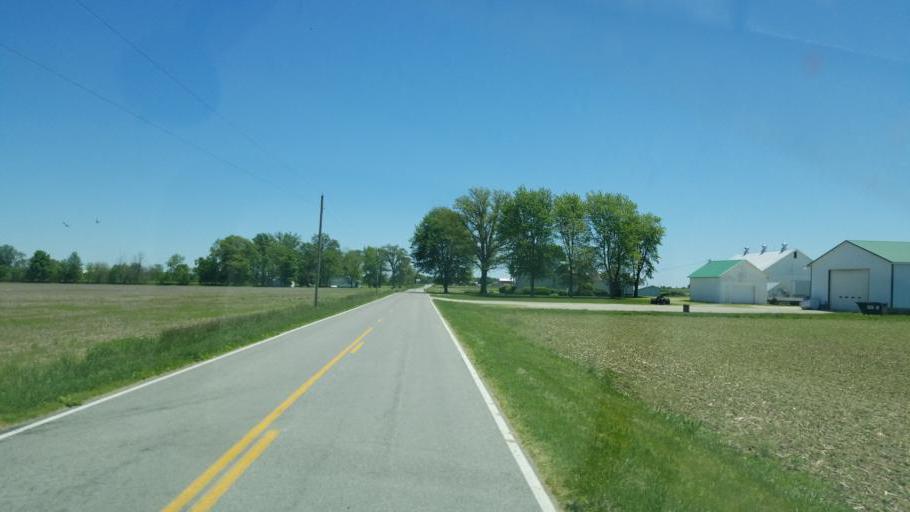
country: US
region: Indiana
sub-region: Randolph County
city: Union City
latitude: 40.2819
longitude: -84.7893
